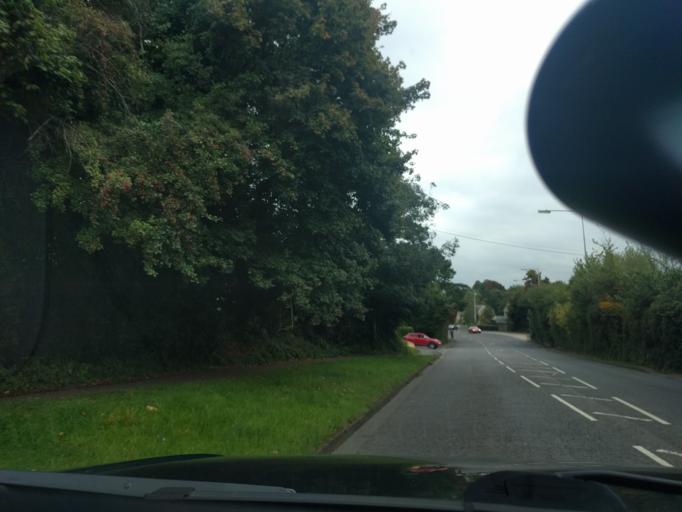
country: GB
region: England
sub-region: Wiltshire
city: Chippenham
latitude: 51.4559
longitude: -2.1235
